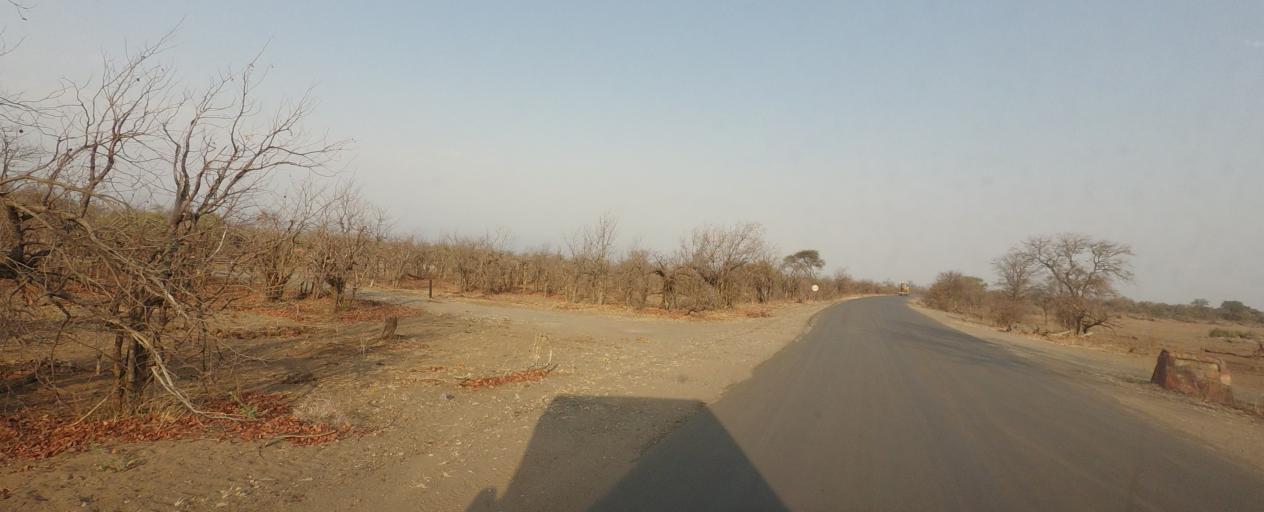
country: ZA
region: Limpopo
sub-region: Mopani District Municipality
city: Giyani
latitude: -23.1075
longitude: 31.4334
